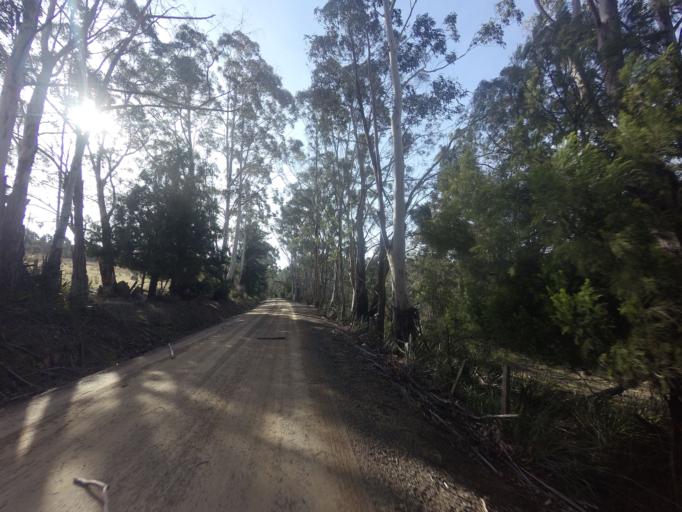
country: AU
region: Tasmania
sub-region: Kingborough
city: Kettering
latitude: -43.1054
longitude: 147.2598
